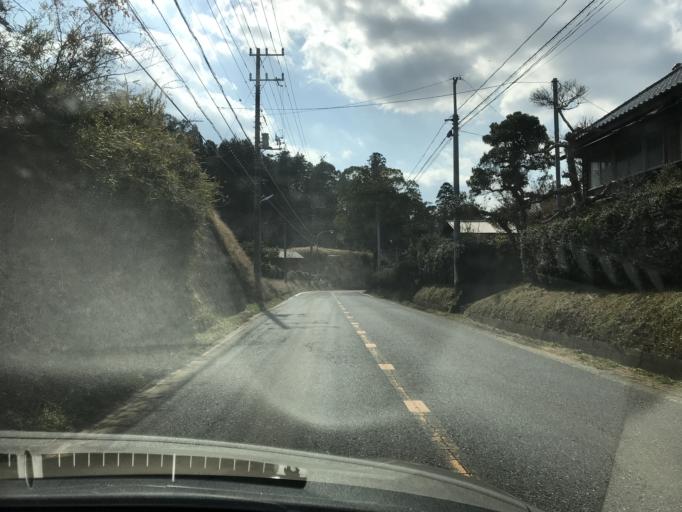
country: JP
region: Chiba
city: Sawara
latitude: 35.8133
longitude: 140.5038
